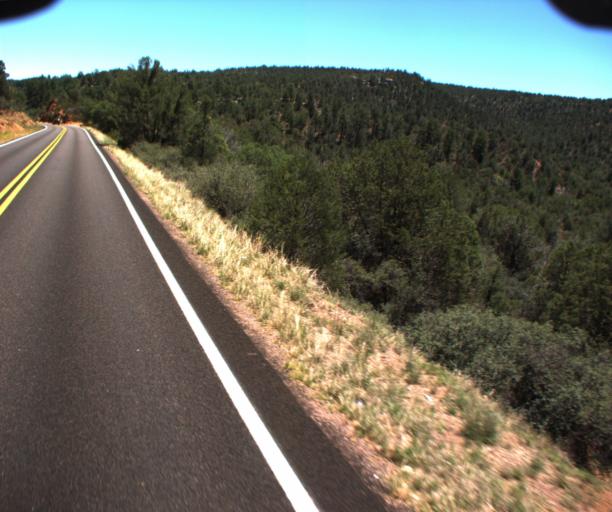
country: US
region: Arizona
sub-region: Gila County
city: Payson
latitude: 34.2873
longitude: -111.3409
